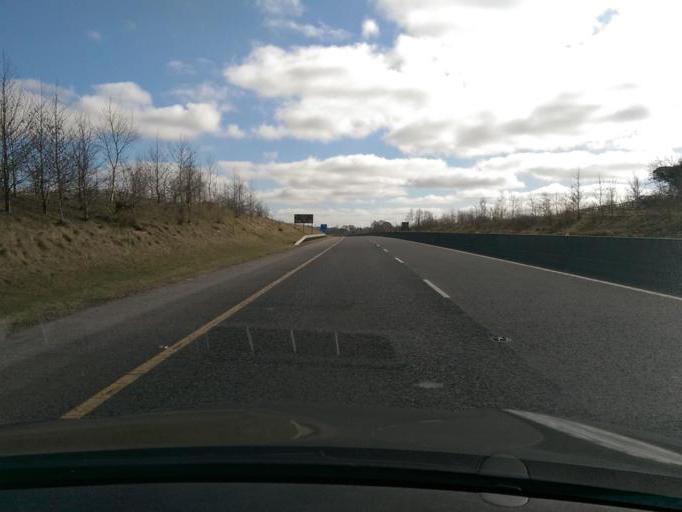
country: IE
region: Leinster
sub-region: An Iarmhi
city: Moate
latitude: 53.3951
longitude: -7.8060
